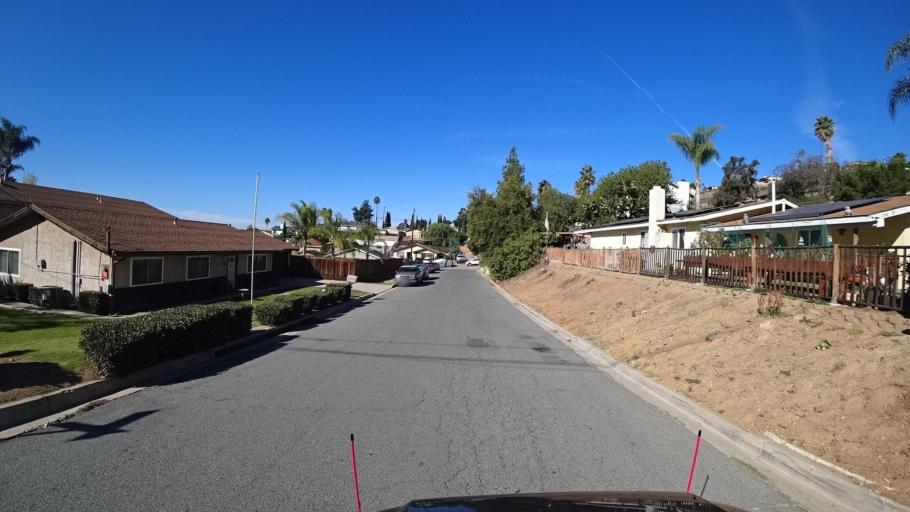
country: US
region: California
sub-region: San Diego County
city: La Presa
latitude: 32.7166
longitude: -116.9894
